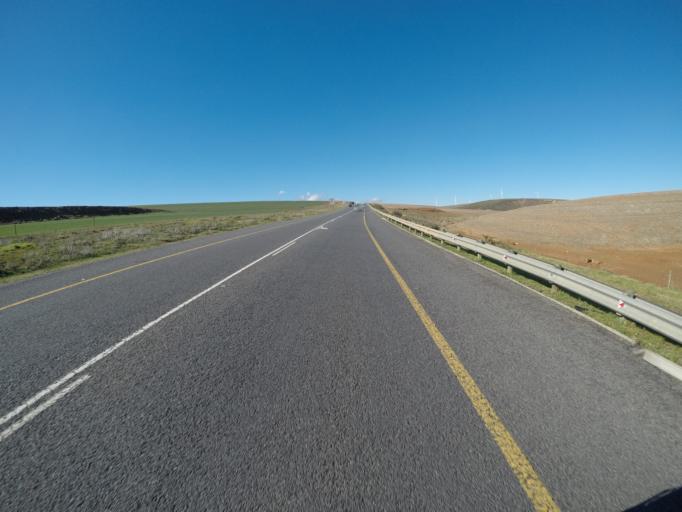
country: ZA
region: Western Cape
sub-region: Overberg District Municipality
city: Caledon
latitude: -34.2108
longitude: 19.3436
